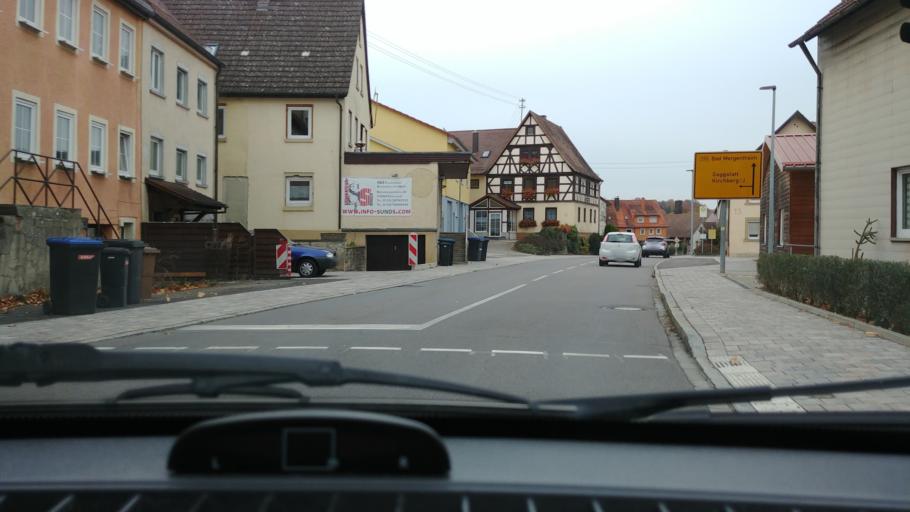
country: DE
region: Baden-Wuerttemberg
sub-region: Regierungsbezirk Stuttgart
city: Wallhausen
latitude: 49.2096
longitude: 10.0638
